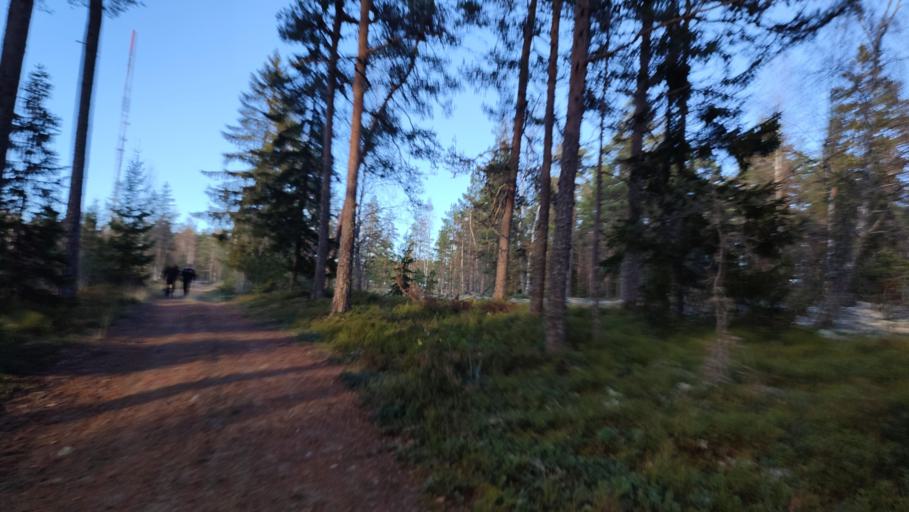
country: FI
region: Southern Ostrobothnia
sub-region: Suupohja
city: Karijoki
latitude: 62.2817
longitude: 21.6438
